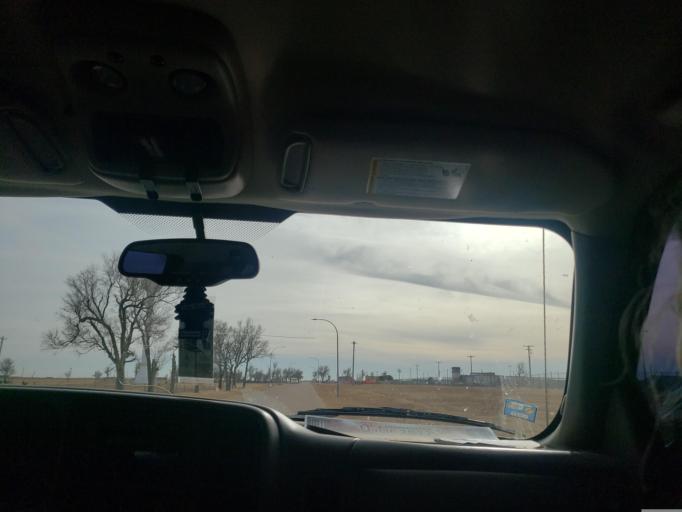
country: US
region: Kansas
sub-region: Finney County
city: Garden City
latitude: 37.9319
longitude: -100.7179
